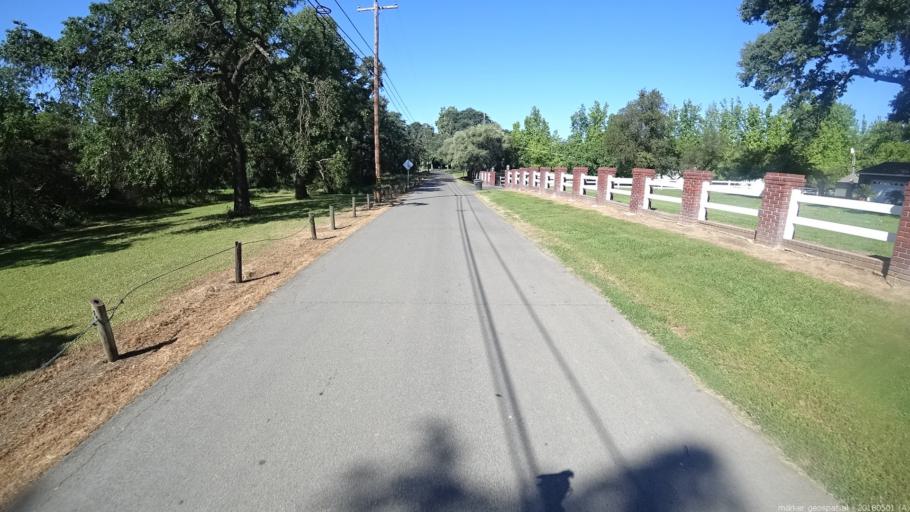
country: US
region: California
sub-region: Sacramento County
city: Arden-Arcade
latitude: 38.6434
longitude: -121.3750
